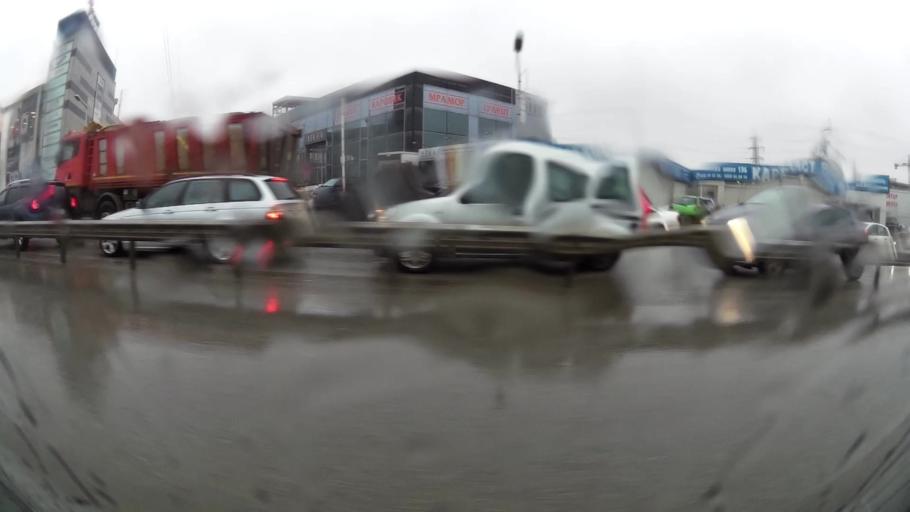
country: BG
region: Sofia-Capital
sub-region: Stolichna Obshtina
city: Sofia
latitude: 42.6339
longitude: 23.3338
